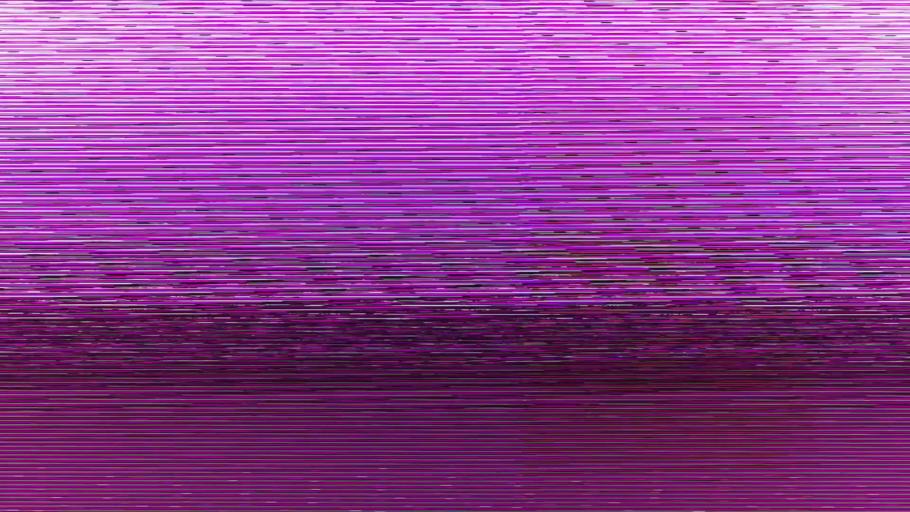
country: US
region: Michigan
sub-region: Oakland County
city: Berkley
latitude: 42.5124
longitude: -83.1811
